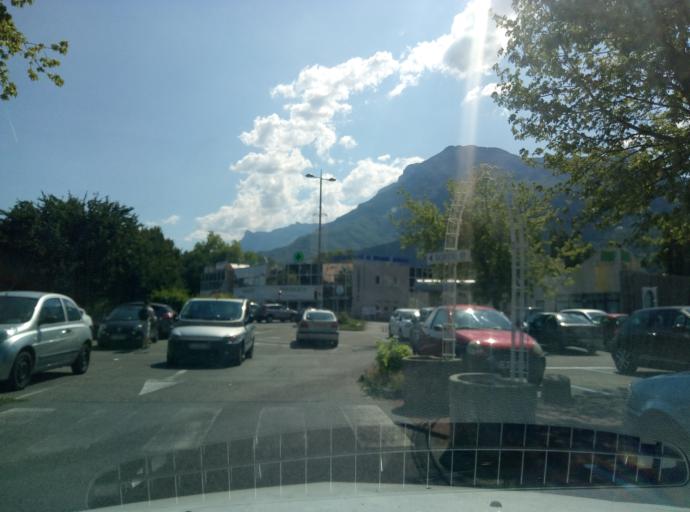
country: FR
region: Rhone-Alpes
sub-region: Departement de l'Isere
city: Seyssinet-Pariset
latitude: 45.1762
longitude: 5.6938
